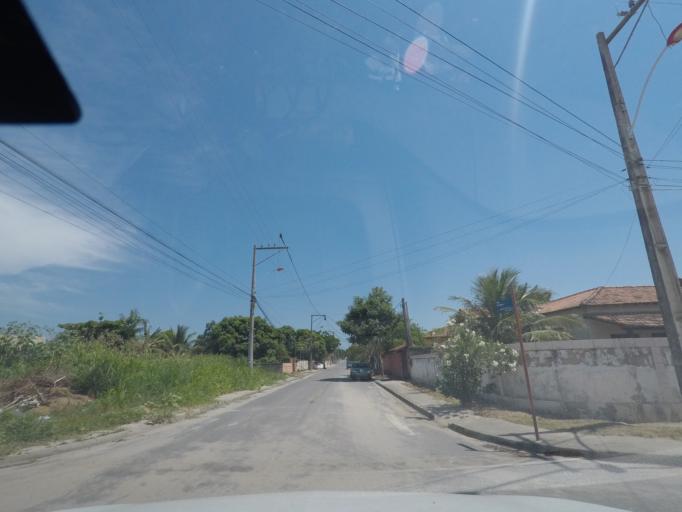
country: BR
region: Rio de Janeiro
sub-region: Marica
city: Marica
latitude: -22.9620
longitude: -42.9568
